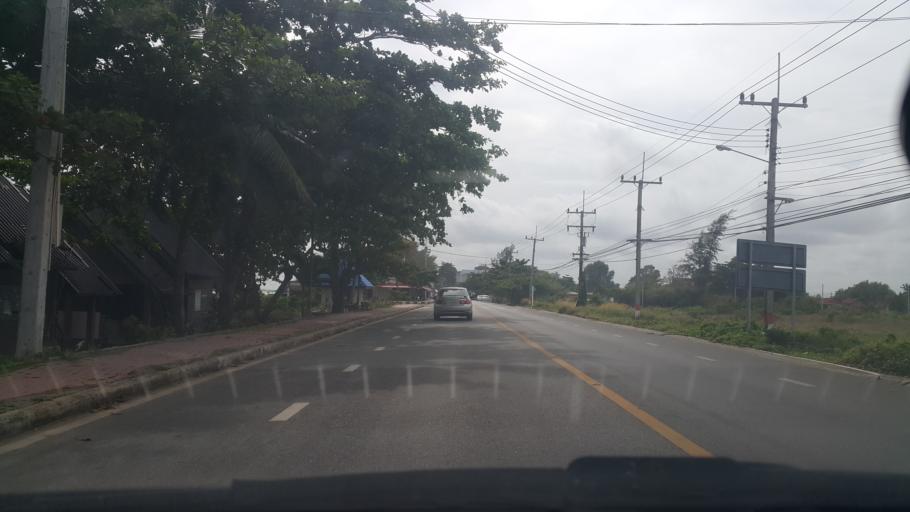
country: TH
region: Rayong
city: Rayong
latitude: 12.6267
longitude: 101.3542
